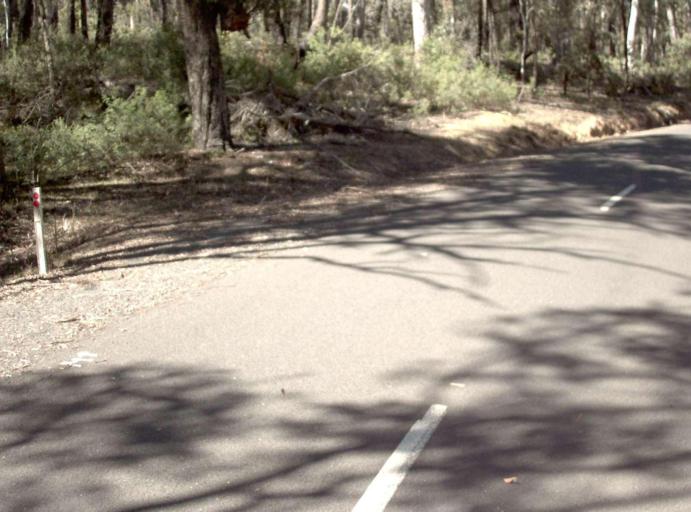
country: AU
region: New South Wales
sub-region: Bombala
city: Bombala
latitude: -37.1103
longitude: 148.7572
